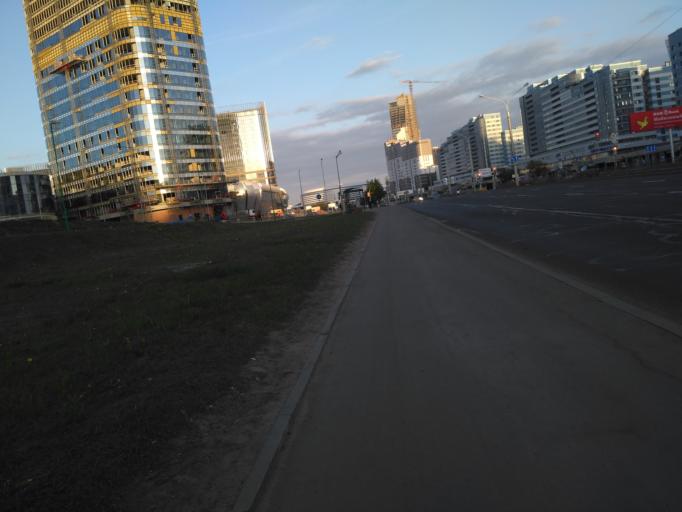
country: BY
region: Minsk
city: Zhdanovichy
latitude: 53.9415
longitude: 27.4680
